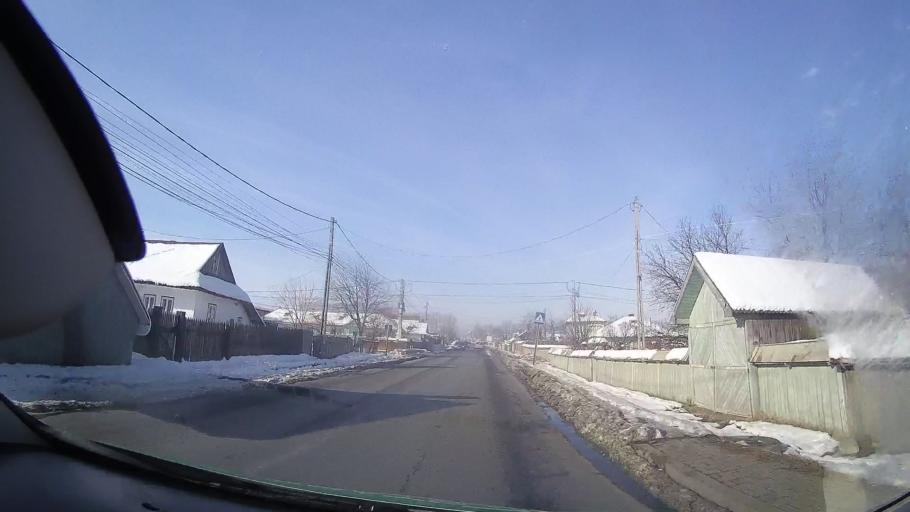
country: RO
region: Neamt
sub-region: Oras Targu Neamt
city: Humulesti
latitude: 47.2015
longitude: 26.3433
